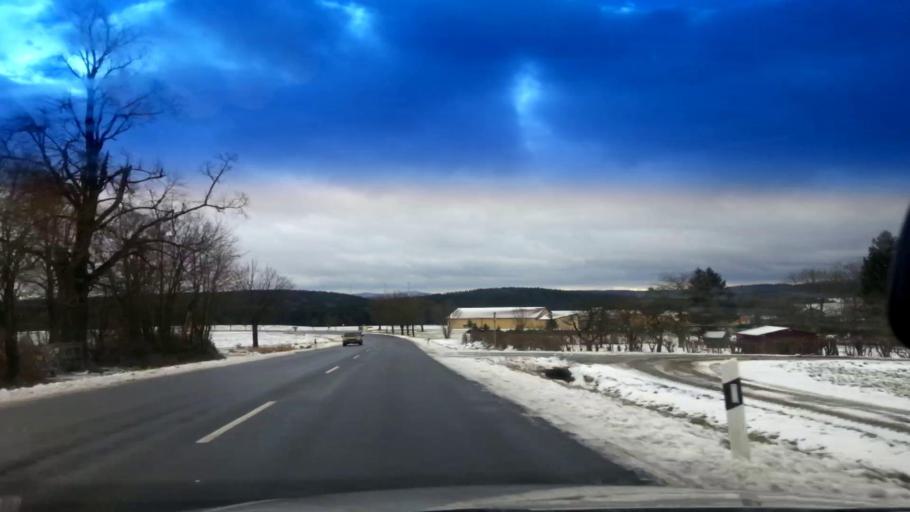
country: DE
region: Bavaria
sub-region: Upper Franconia
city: Kirchenlamitz
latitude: 50.1400
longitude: 11.9691
